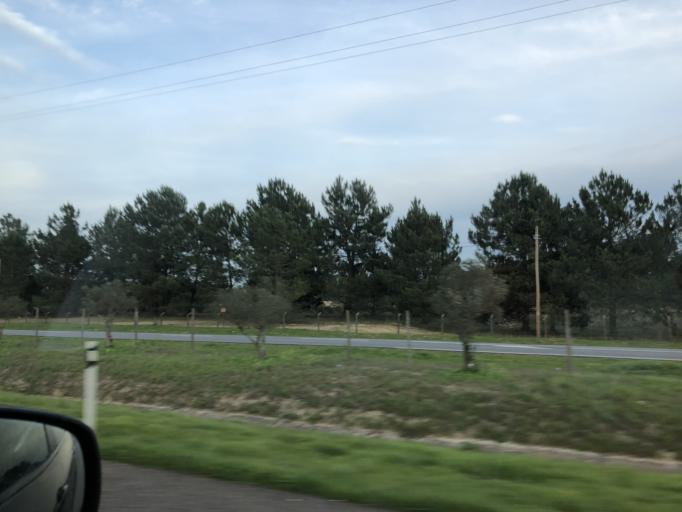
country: PT
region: Setubal
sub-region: Palmela
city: Pinhal Novo
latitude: 38.6748
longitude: -8.8939
